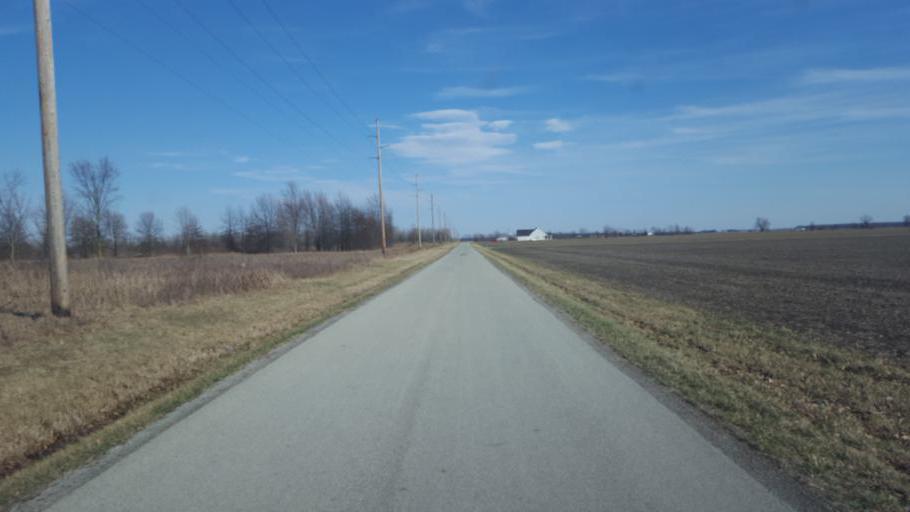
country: US
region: Ohio
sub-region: Wyandot County
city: Upper Sandusky
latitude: 40.6944
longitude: -83.3190
